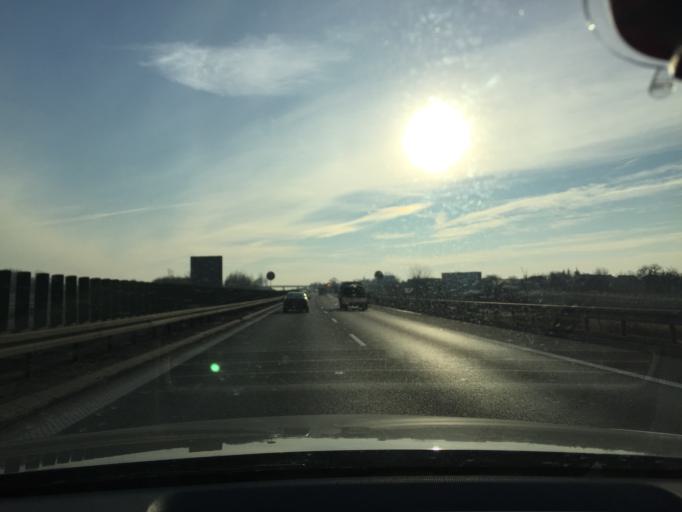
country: PL
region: Lesser Poland Voivodeship
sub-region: Powiat krakowski
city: Balice
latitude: 50.0674
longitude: 19.8104
